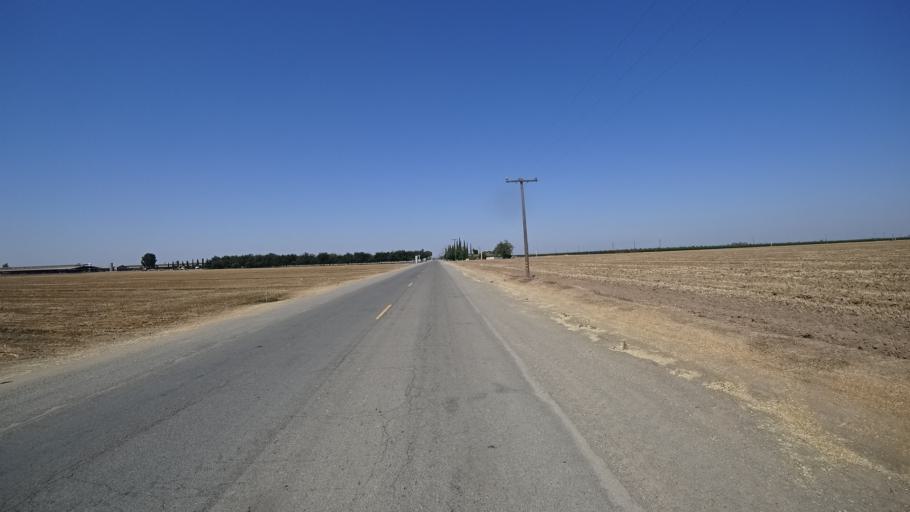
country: US
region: California
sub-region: Kings County
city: Hanford
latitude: 36.3719
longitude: -119.5706
